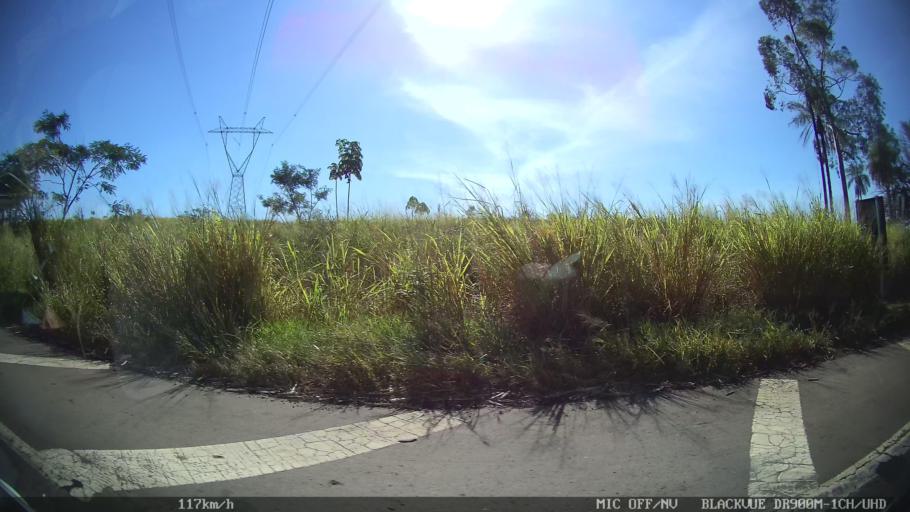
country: BR
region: Sao Paulo
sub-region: Olimpia
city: Olimpia
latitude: -20.6322
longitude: -48.8134
